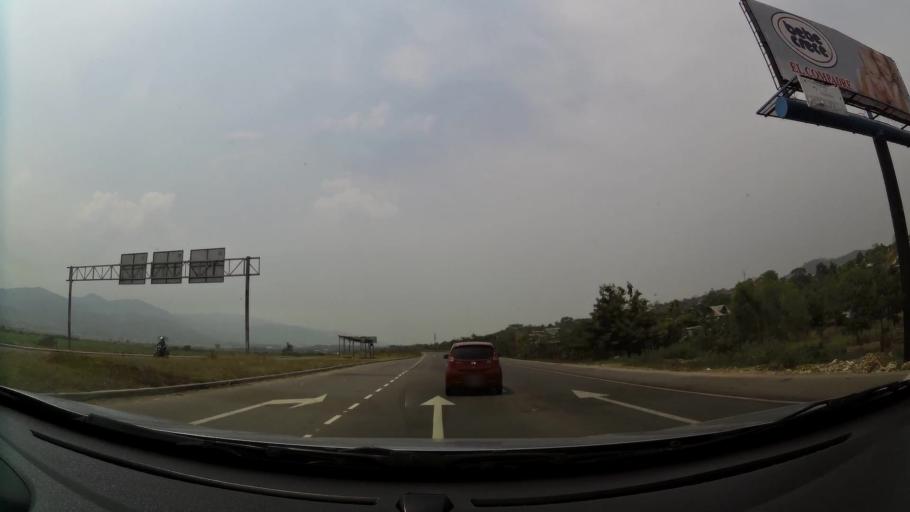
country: HN
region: Cortes
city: El Plan
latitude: 15.2858
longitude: -87.9774
